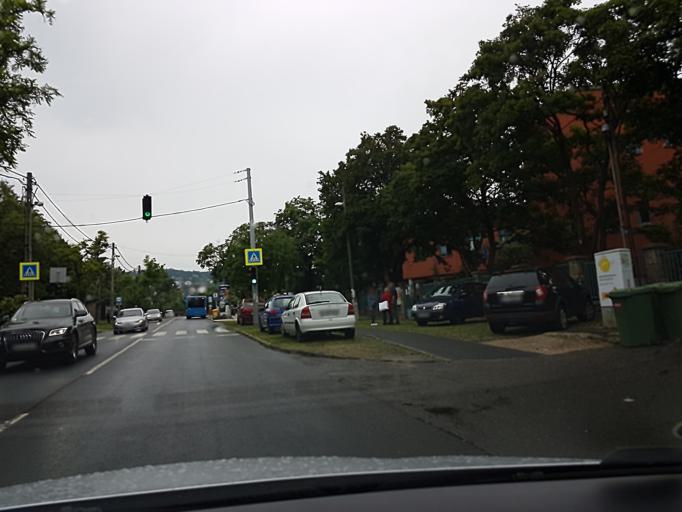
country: HU
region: Budapest
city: Budapest II. keruelet
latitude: 47.5268
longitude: 19.0081
